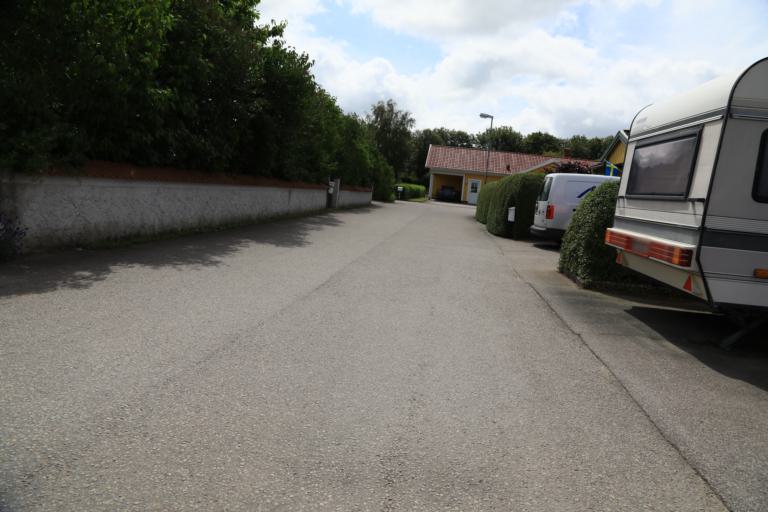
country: SE
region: Halland
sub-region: Varbergs Kommun
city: Varberg
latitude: 57.1121
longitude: 12.2944
